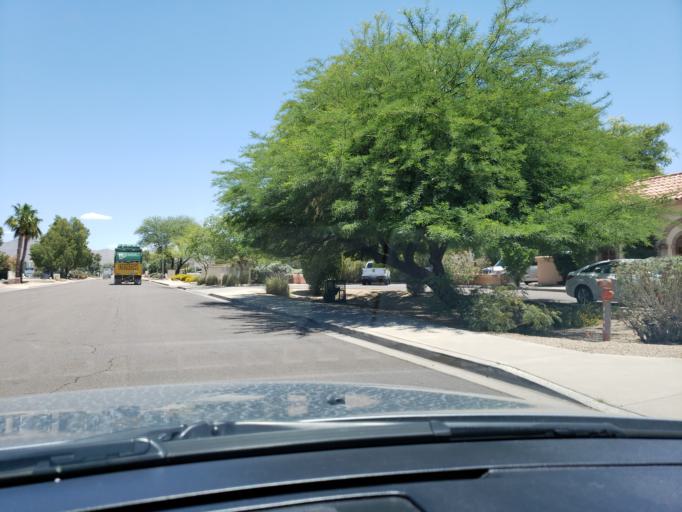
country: US
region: Arizona
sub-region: Maricopa County
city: Paradise Valley
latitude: 33.6165
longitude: -111.9135
